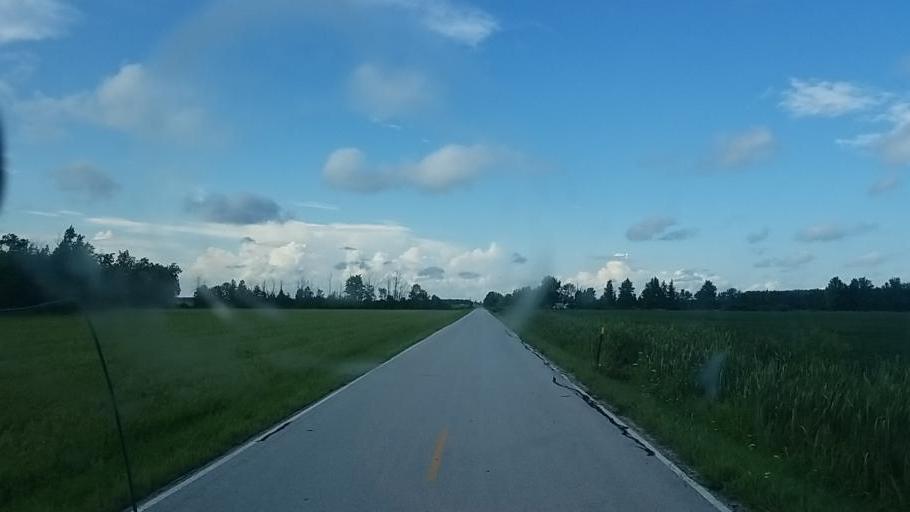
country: US
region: Ohio
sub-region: Hardin County
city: Forest
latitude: 40.7495
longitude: -83.4966
